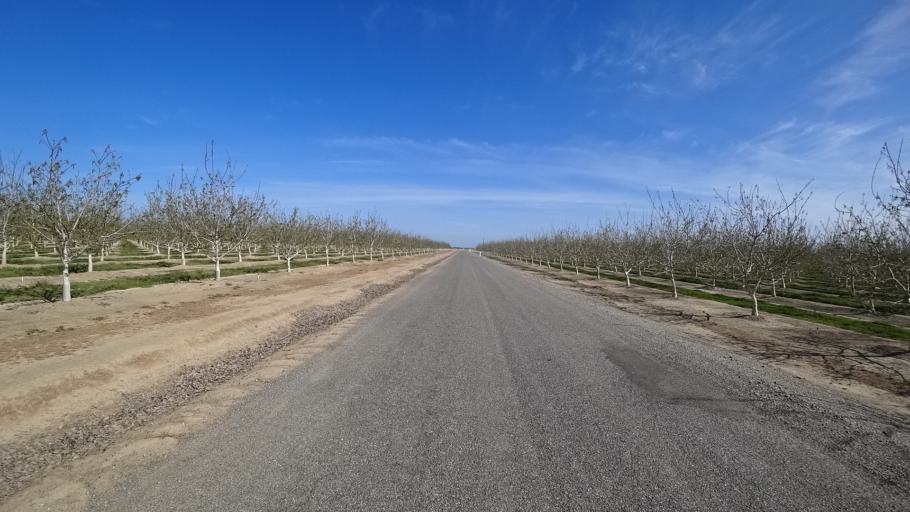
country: US
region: California
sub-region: Glenn County
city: Willows
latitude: 39.6205
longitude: -122.1170
